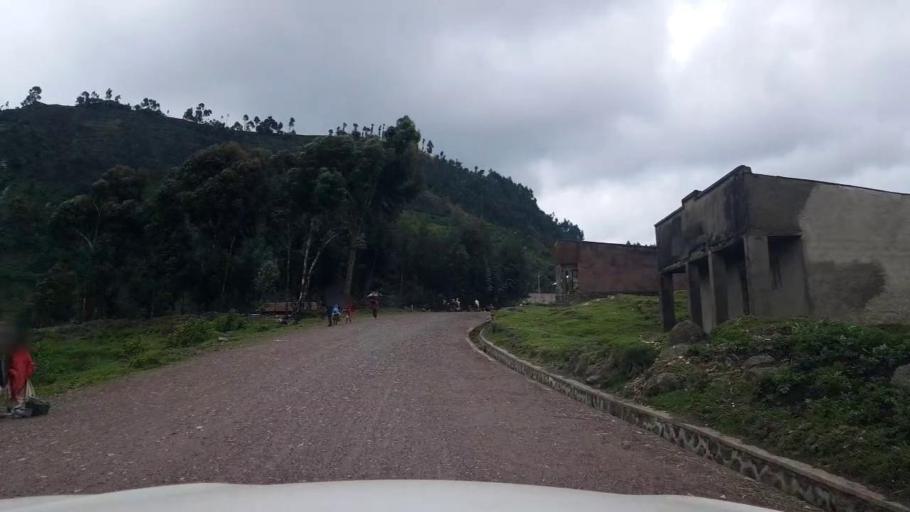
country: RW
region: Northern Province
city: Musanze
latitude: -1.5901
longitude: 29.4681
